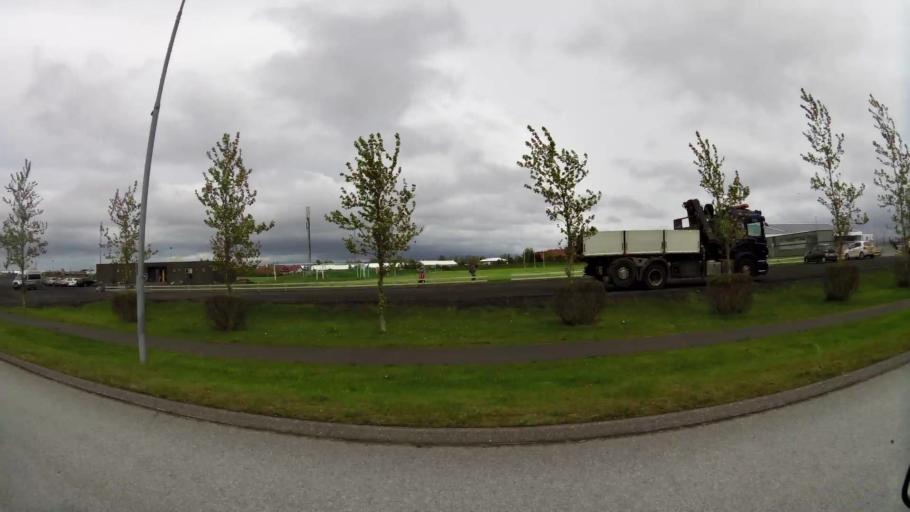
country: IS
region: Capital Region
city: Alftanes
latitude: 64.1044
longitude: -22.0216
